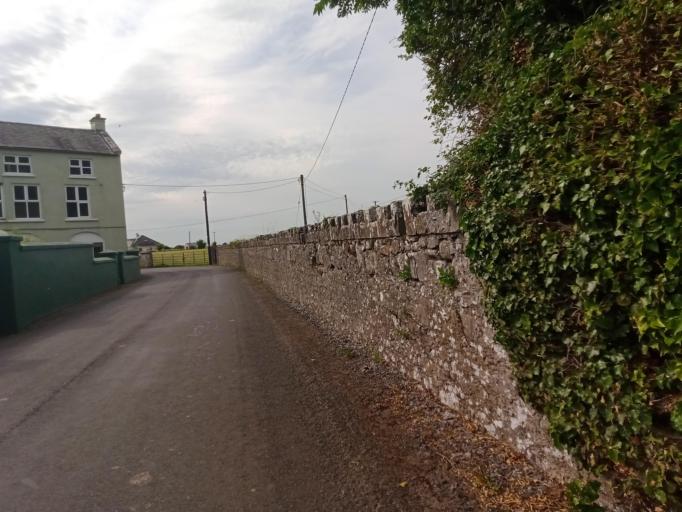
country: IE
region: Leinster
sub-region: Laois
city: Rathdowney
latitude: 52.8223
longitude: -7.4809
